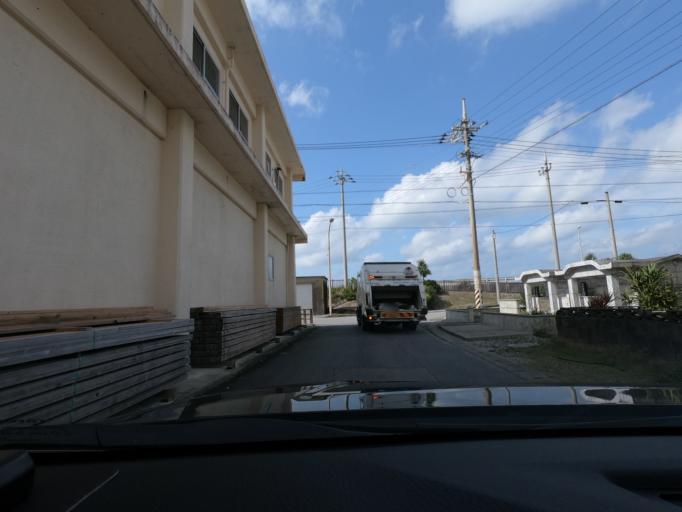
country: JP
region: Okinawa
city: Nago
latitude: 26.7569
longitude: 128.1894
